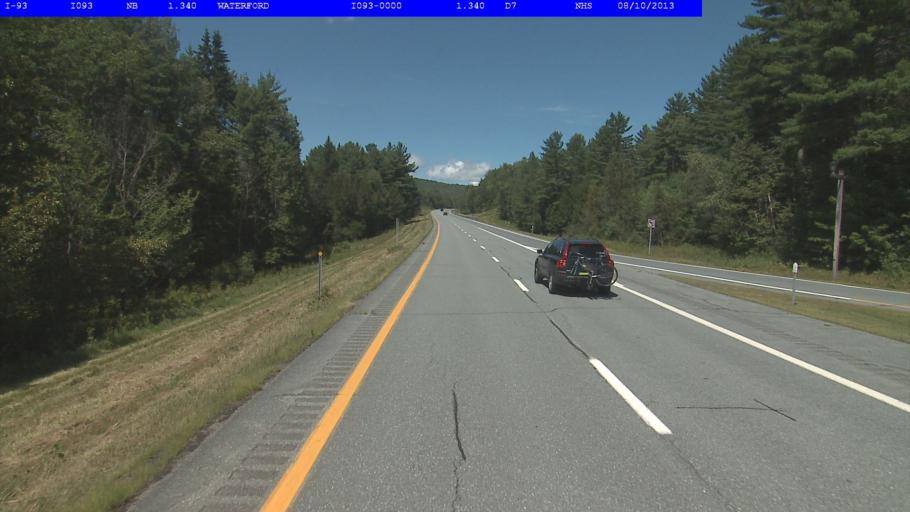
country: US
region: Vermont
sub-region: Caledonia County
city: Saint Johnsbury
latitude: 44.3616
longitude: -71.8989
